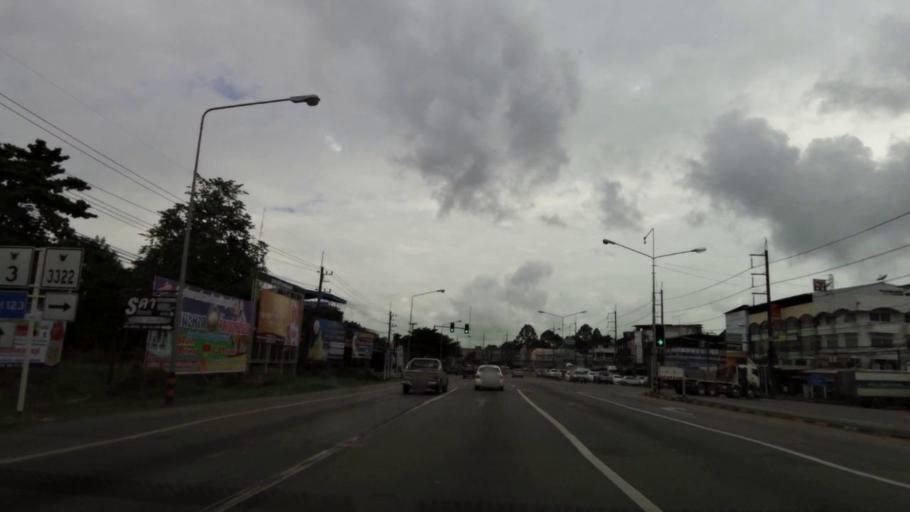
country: TH
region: Chanthaburi
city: Tha Mai
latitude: 12.7206
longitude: 101.9732
